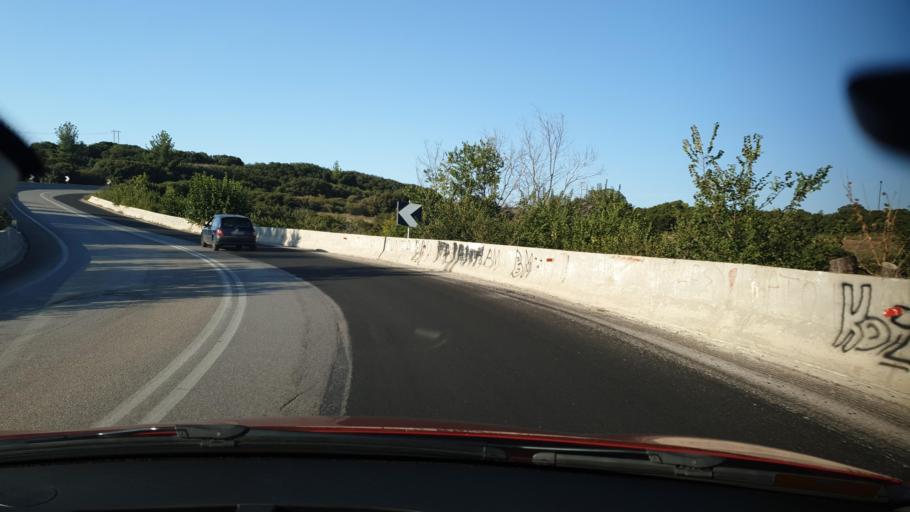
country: GR
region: Central Macedonia
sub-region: Nomos Thessalonikis
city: Panorama
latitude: 40.6133
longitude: 23.0602
